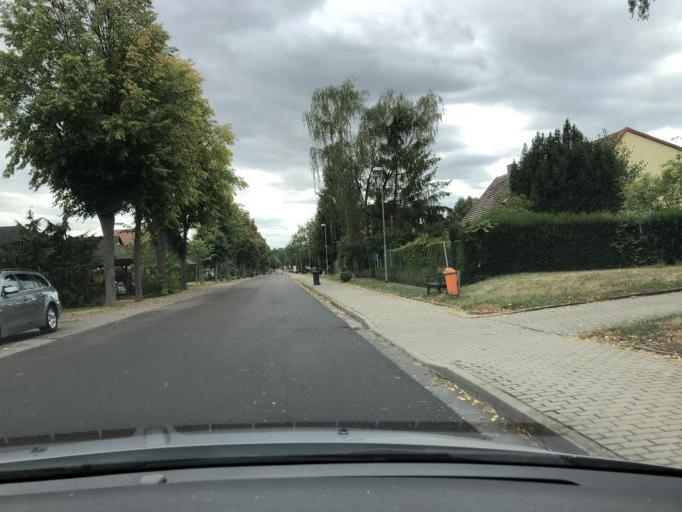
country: DE
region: Saxony-Anhalt
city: Brumby
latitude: 51.8564
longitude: 11.7102
